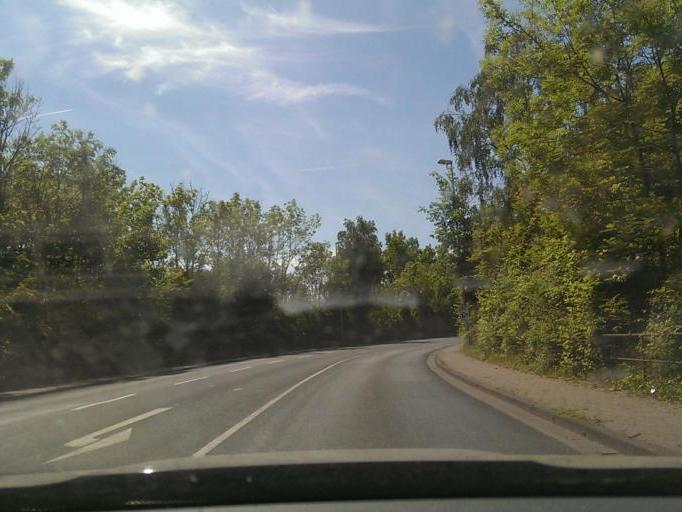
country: DE
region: Lower Saxony
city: Alfeld
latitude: 51.9809
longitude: 9.8213
